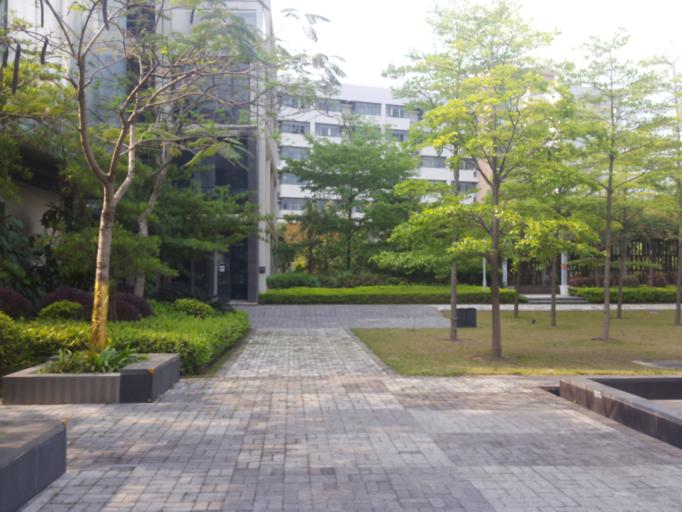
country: CN
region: Guangdong
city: Wanzai
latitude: 22.1580
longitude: 113.4724
